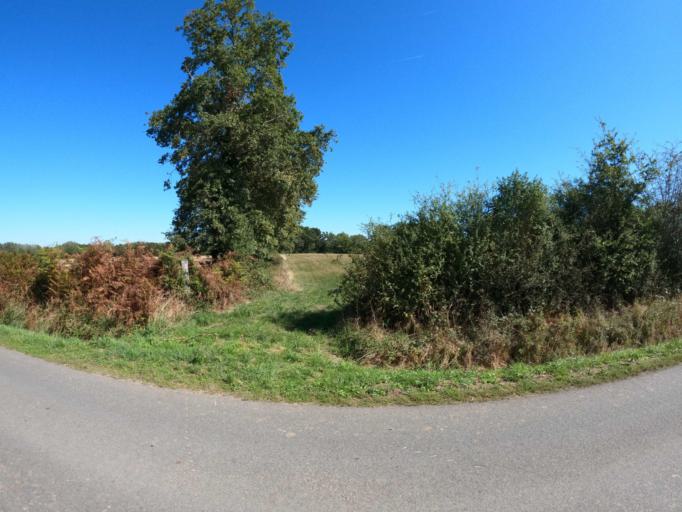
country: FR
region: Limousin
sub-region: Departement de la Haute-Vienne
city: Le Dorat
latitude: 46.2464
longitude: 1.0491
